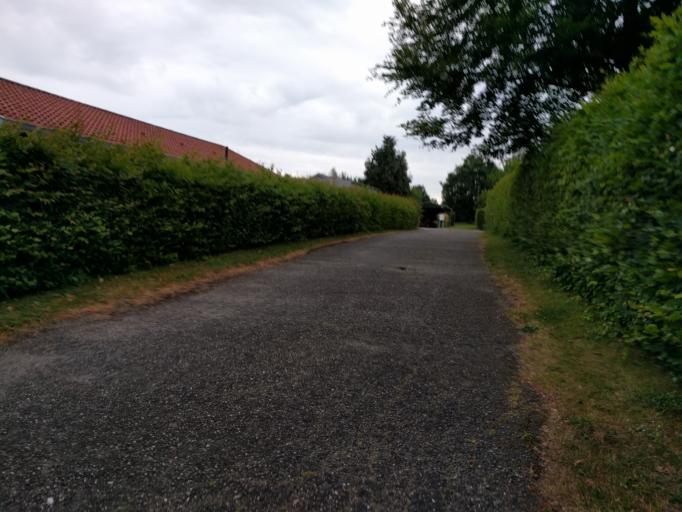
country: DK
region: South Denmark
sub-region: Kerteminde Kommune
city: Munkebo
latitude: 55.4471
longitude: 10.5491
